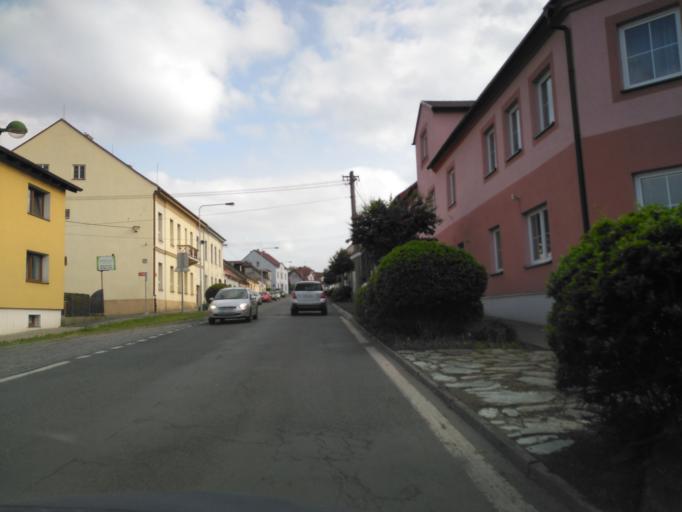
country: CZ
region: Plzensky
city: Zbiroh
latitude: 49.8585
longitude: 13.7692
